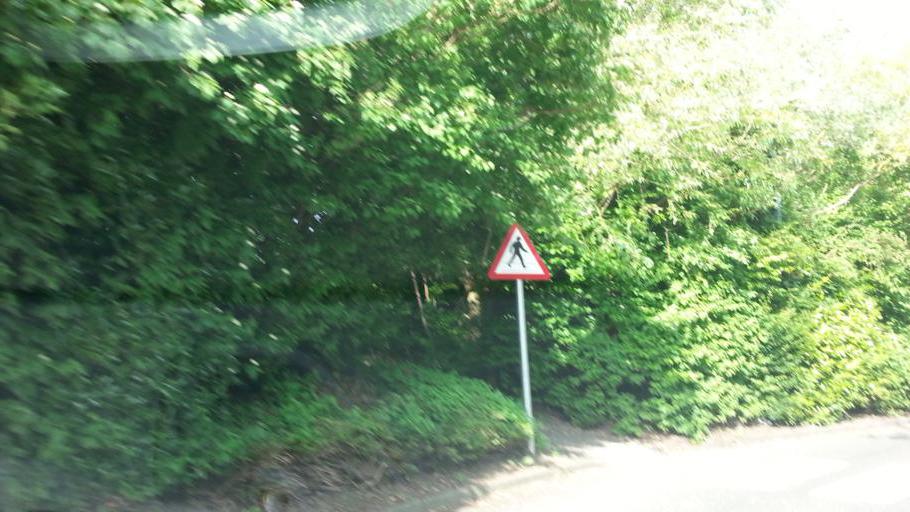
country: GB
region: England
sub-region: Nottinghamshire
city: West Bridgford
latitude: 52.9233
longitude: -1.1020
